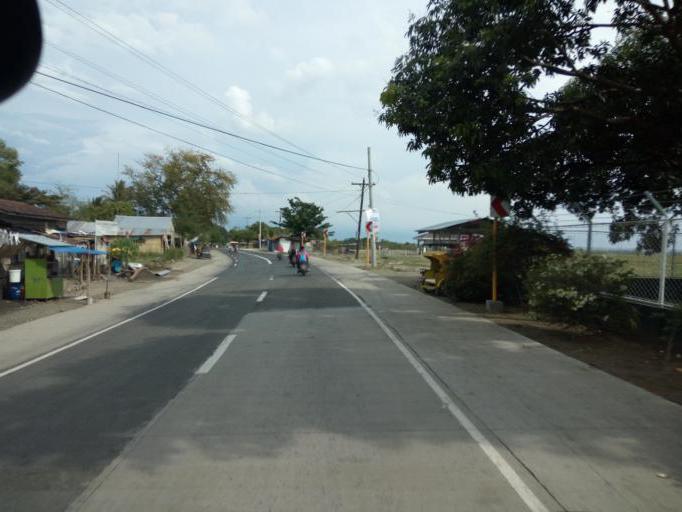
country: PH
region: Central Luzon
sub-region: Province of Nueva Ecija
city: Parista
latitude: 15.8311
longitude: 120.9457
